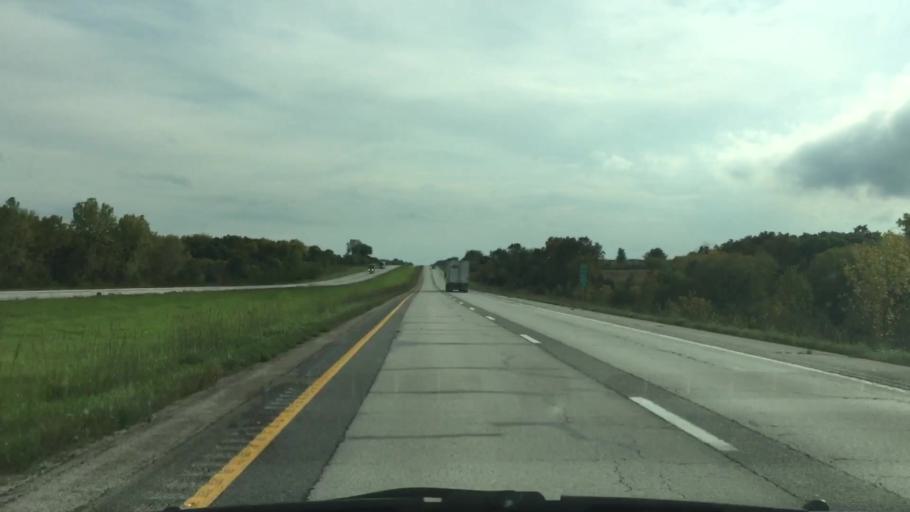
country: US
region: Iowa
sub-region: Decatur County
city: Lamoni
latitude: 40.4485
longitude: -93.9822
